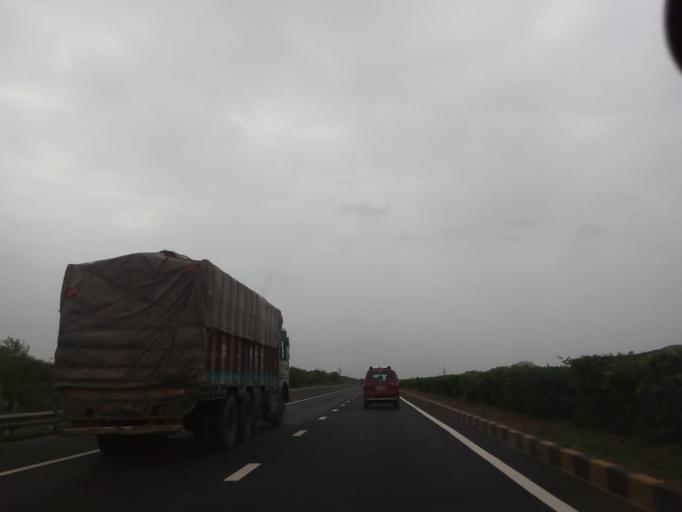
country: IN
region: Gujarat
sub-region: Kheda
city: Mahemdavad
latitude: 22.8025
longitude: 72.8379
